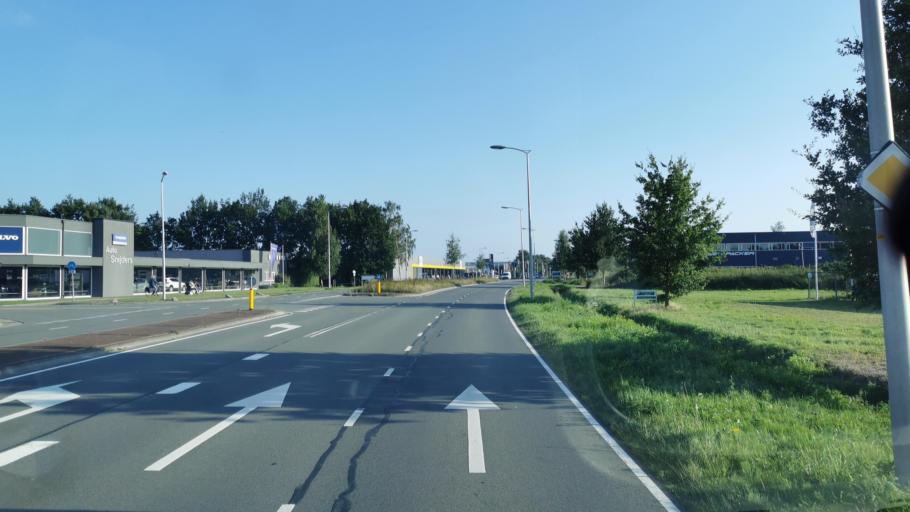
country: NL
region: Overijssel
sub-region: Gemeente Oldenzaal
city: Oldenzaal
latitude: 52.3017
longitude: 6.9231
